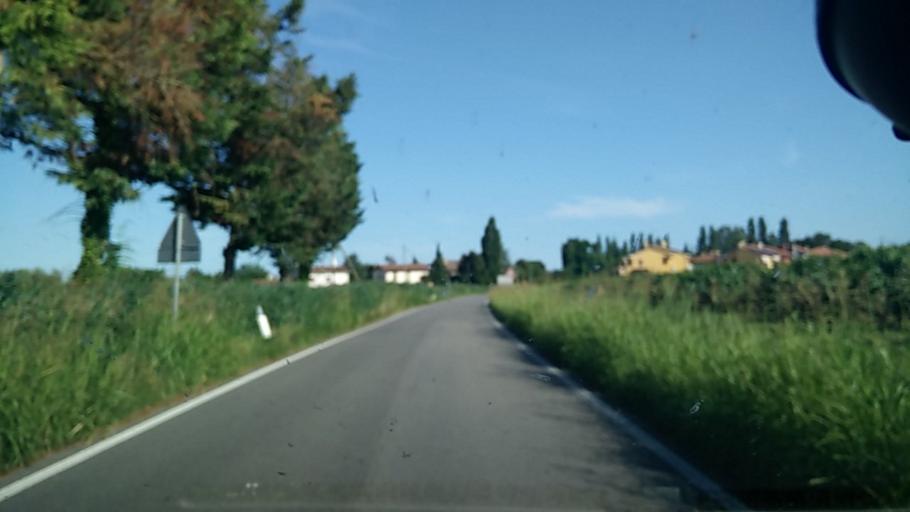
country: IT
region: Veneto
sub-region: Provincia di Treviso
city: San Biagio di Callalta
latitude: 45.6822
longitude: 12.3983
